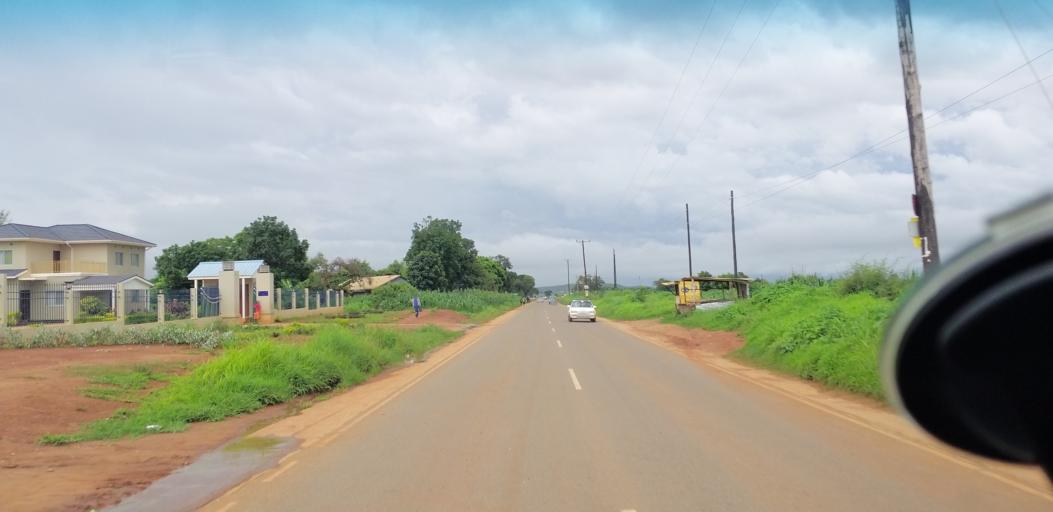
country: ZM
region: Lusaka
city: Lusaka
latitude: -15.5174
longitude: 28.2977
